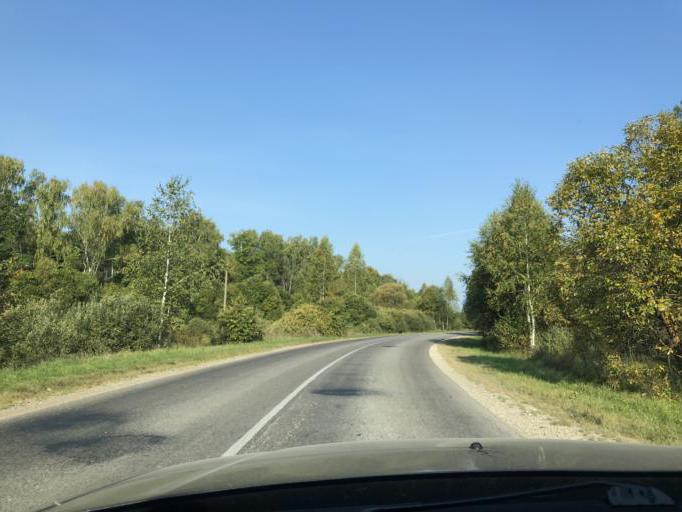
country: RU
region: Tula
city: Leninskiy
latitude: 54.3323
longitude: 37.3852
